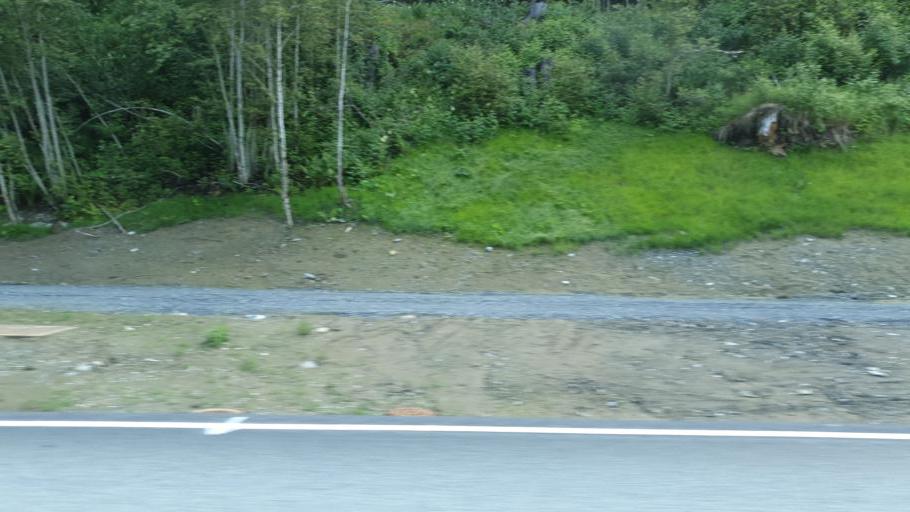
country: NO
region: Sor-Trondelag
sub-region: Midtre Gauldal
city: Storen
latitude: 62.9810
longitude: 10.2348
